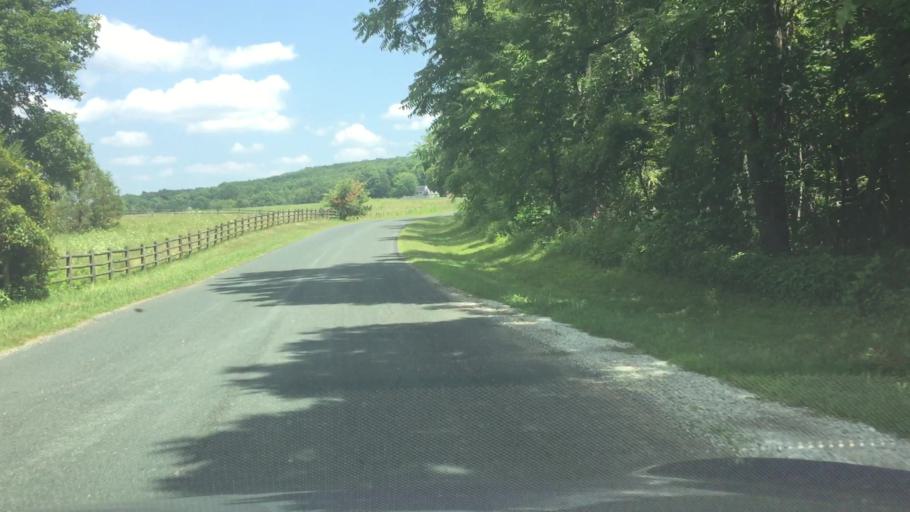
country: US
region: Virginia
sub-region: Appomattox County
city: Appomattox
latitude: 37.3220
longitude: -78.8572
